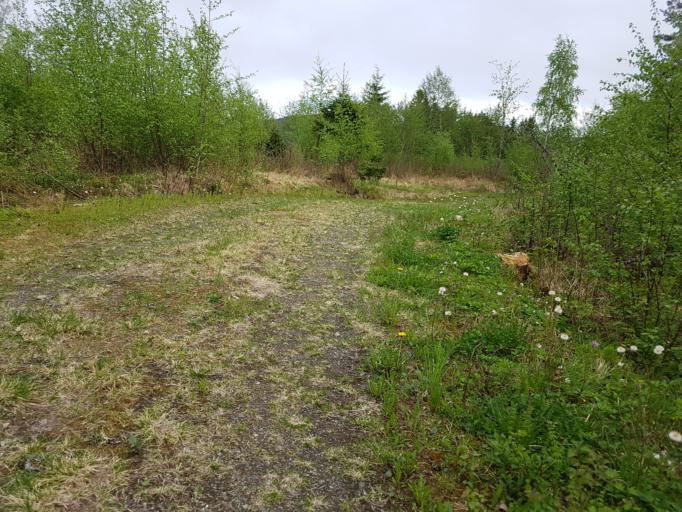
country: NO
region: Nord-Trondelag
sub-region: Levanger
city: Skogn
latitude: 63.6324
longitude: 11.2537
